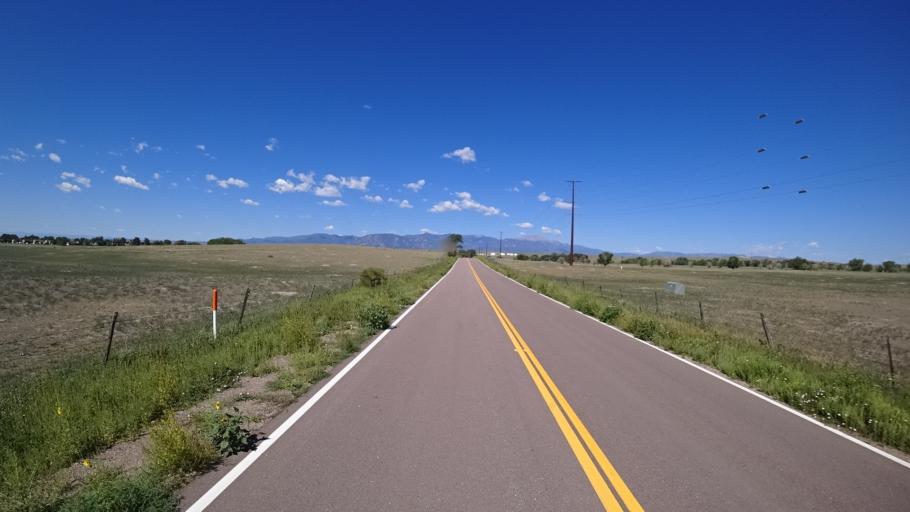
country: US
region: Colorado
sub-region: El Paso County
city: Security-Widefield
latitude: 38.7810
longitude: -104.6425
